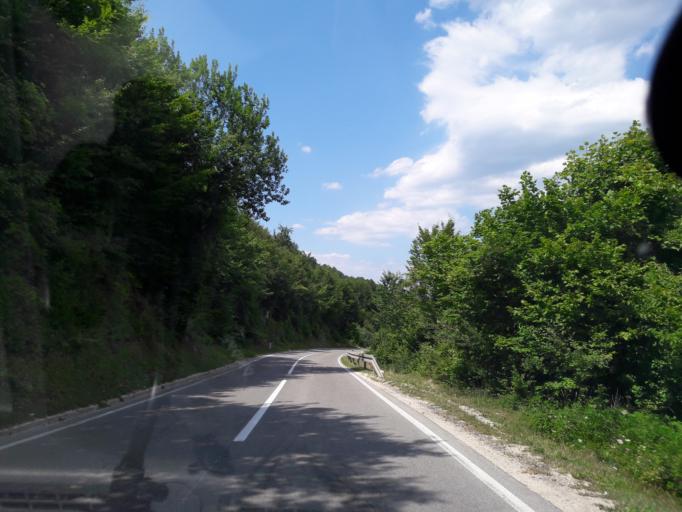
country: BA
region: Republika Srpska
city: Sipovo
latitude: 44.1902
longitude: 17.1582
